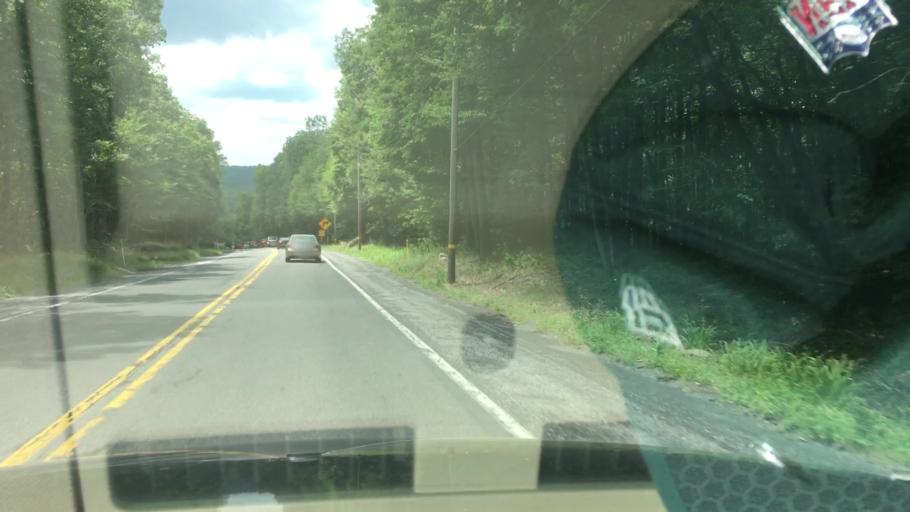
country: US
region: Pennsylvania
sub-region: Schuylkill County
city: Minersville
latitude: 40.7009
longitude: -76.3208
